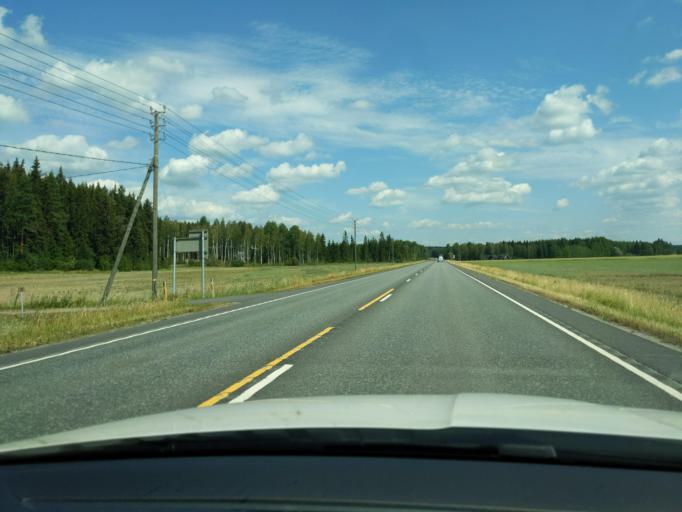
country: FI
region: Uusimaa
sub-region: Helsinki
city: Maentsaelae
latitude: 60.5947
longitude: 25.2480
